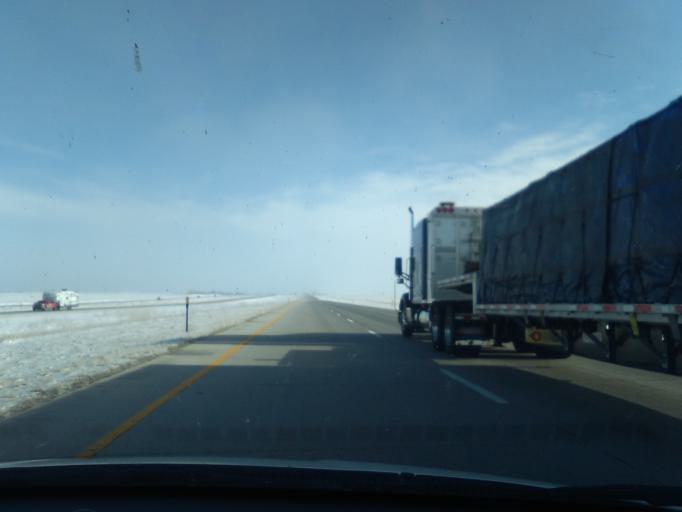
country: US
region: Wyoming
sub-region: Laramie County
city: Pine Bluffs
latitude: 41.1575
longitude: -104.3899
